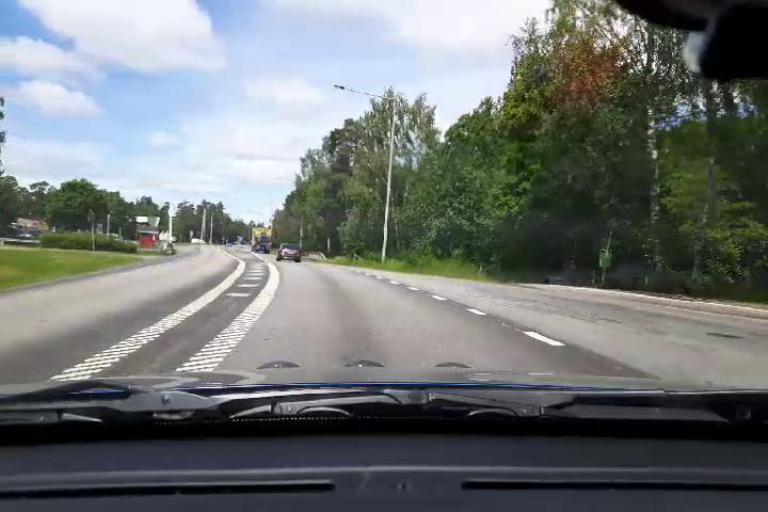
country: SE
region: Uppsala
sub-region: Osthammars Kommun
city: Bjorklinge
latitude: 60.0284
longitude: 17.5536
